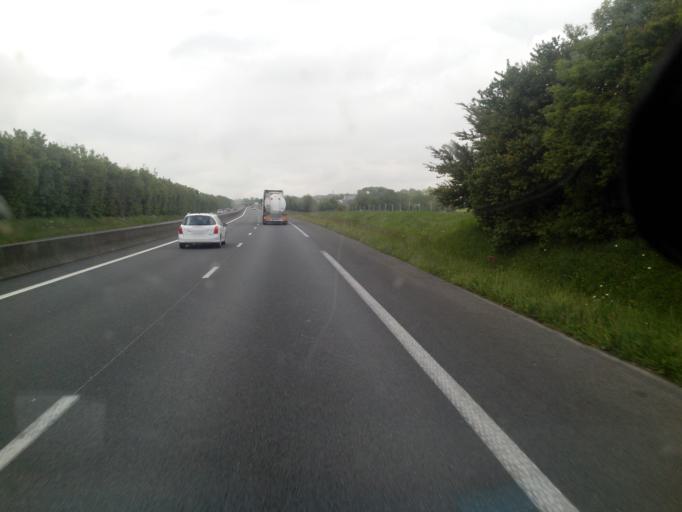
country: FR
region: Lower Normandy
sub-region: Departement du Calvados
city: Villers-Bocage
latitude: 49.0785
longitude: -0.6408
